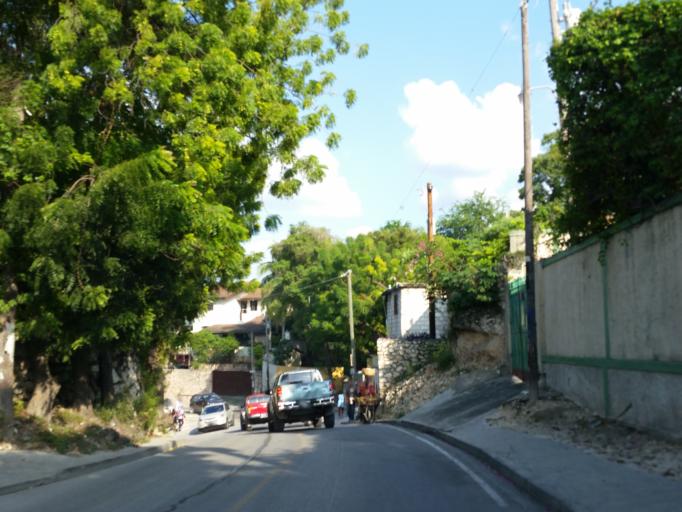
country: HT
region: Ouest
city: Petionville
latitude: 18.5221
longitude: -72.2737
